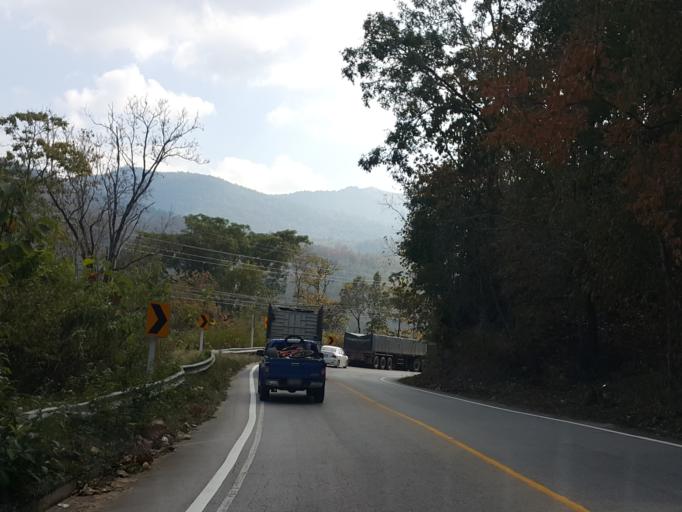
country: TH
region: Chiang Mai
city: Hot
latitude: 18.1982
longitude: 98.4503
